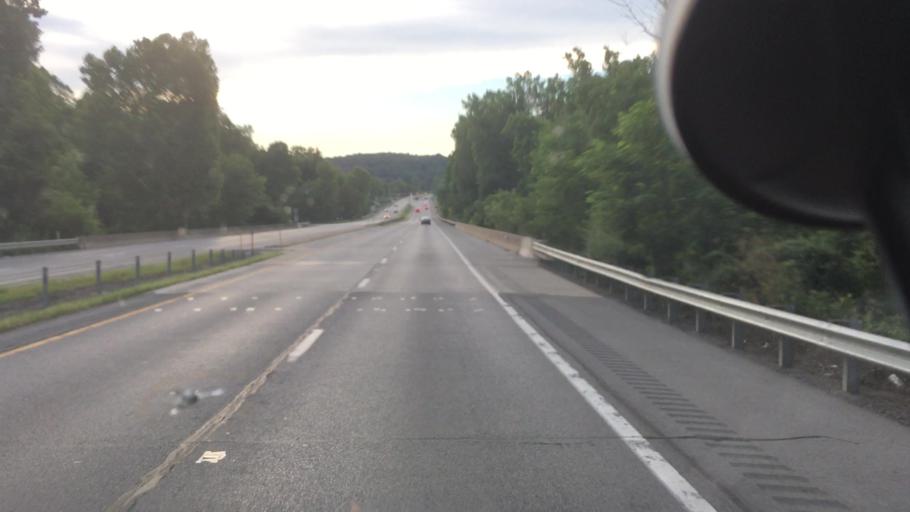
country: US
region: Pennsylvania
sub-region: Beaver County
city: Big Beaver
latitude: 40.8024
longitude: -80.4401
